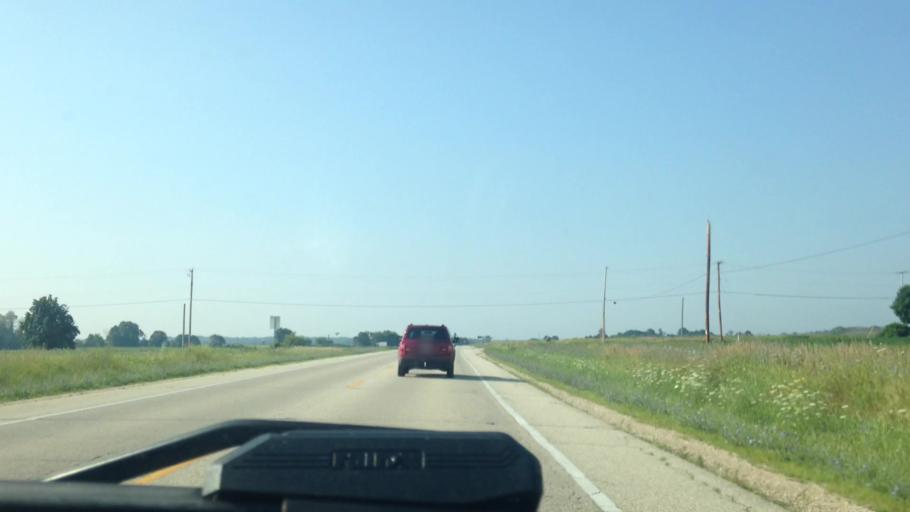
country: US
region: Wisconsin
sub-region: Washington County
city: Slinger
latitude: 43.2826
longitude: -88.2611
